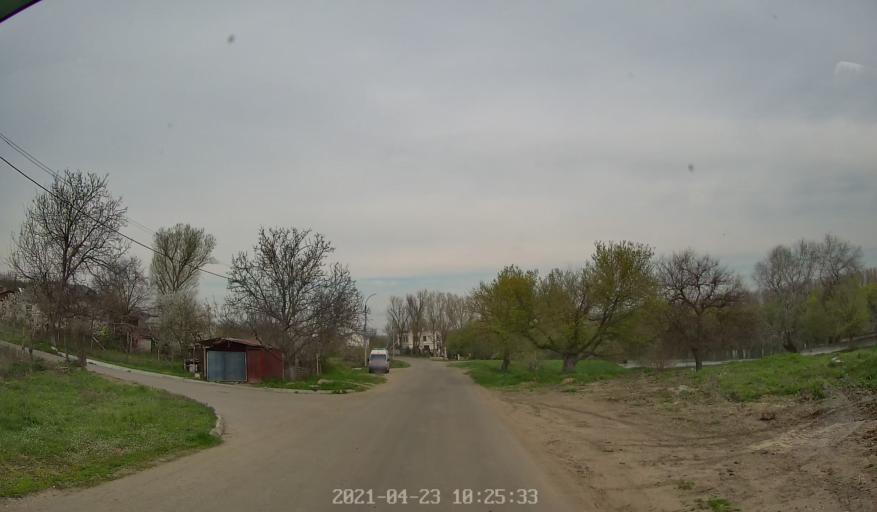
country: MD
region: Chisinau
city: Vadul lui Voda
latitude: 47.0916
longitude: 29.0807
